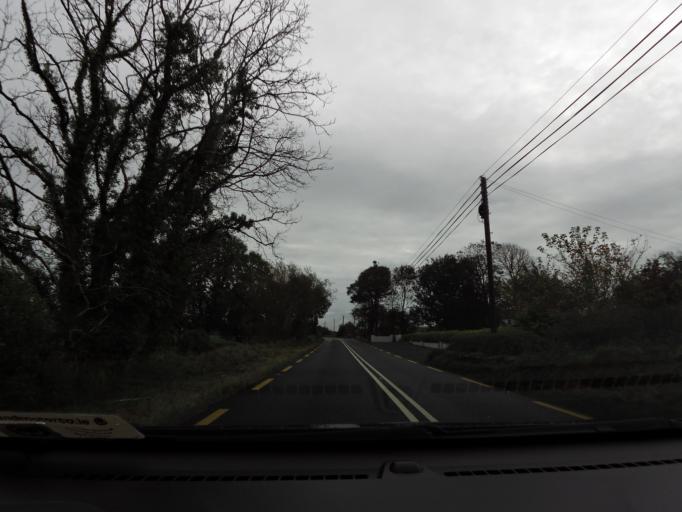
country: IE
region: Connaught
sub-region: County Galway
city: Tuam
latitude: 53.6010
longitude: -8.7614
